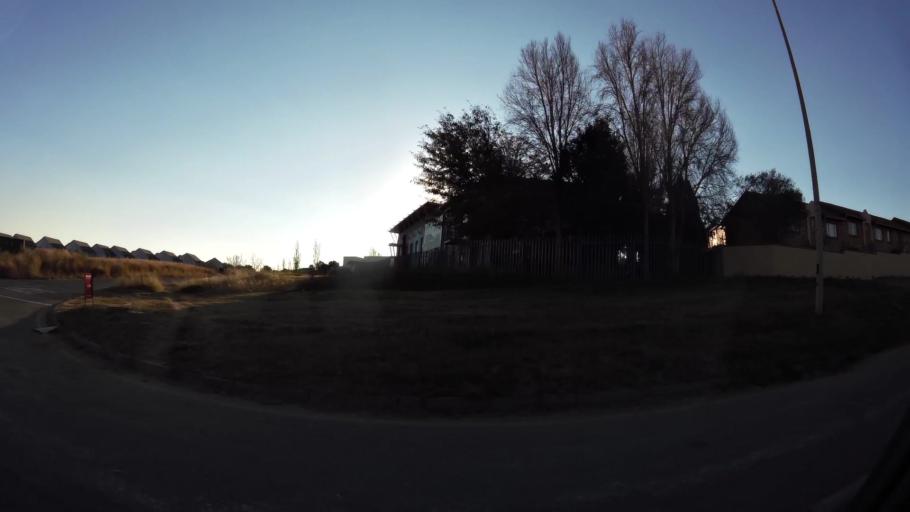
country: ZA
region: Gauteng
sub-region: City of Johannesburg Metropolitan Municipality
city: Midrand
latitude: -25.9925
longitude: 28.1199
